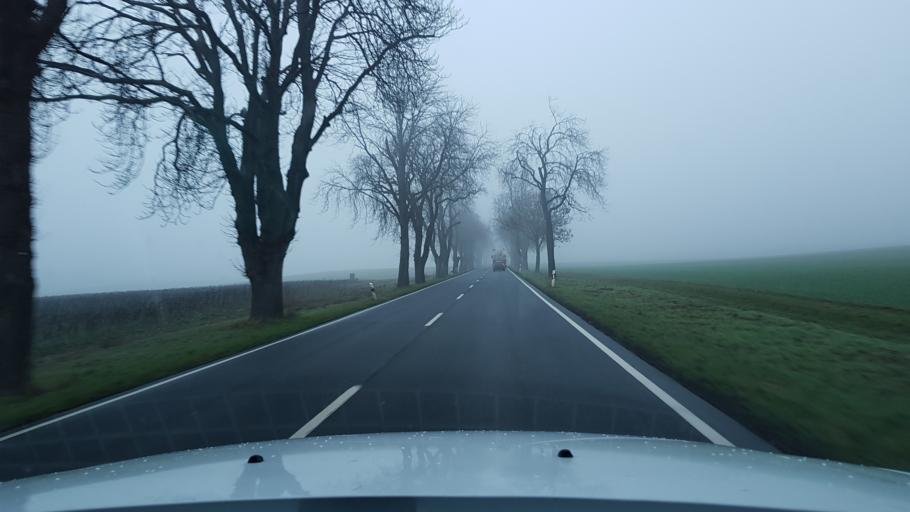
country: DE
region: Brandenburg
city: Mescherin
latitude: 53.2894
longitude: 14.4069
